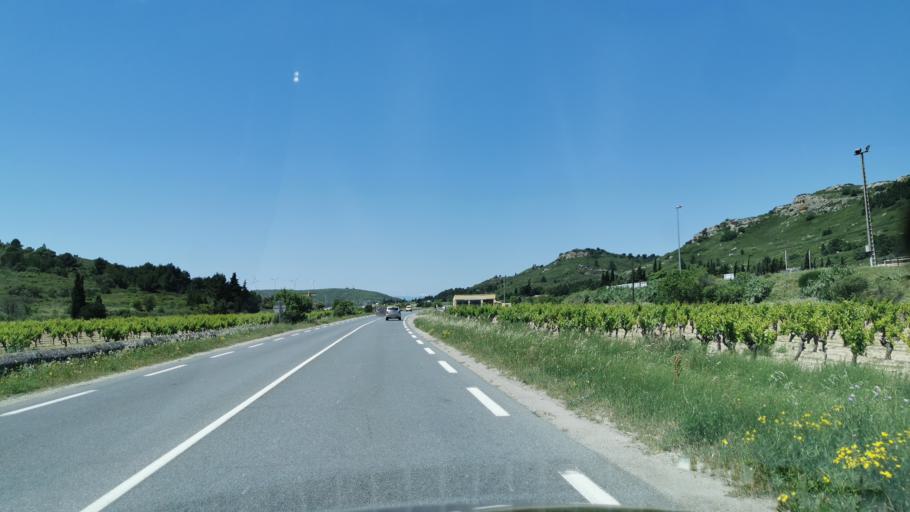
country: FR
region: Languedoc-Roussillon
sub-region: Departement de l'Aude
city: Nevian
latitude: 43.1868
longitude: 2.9163
